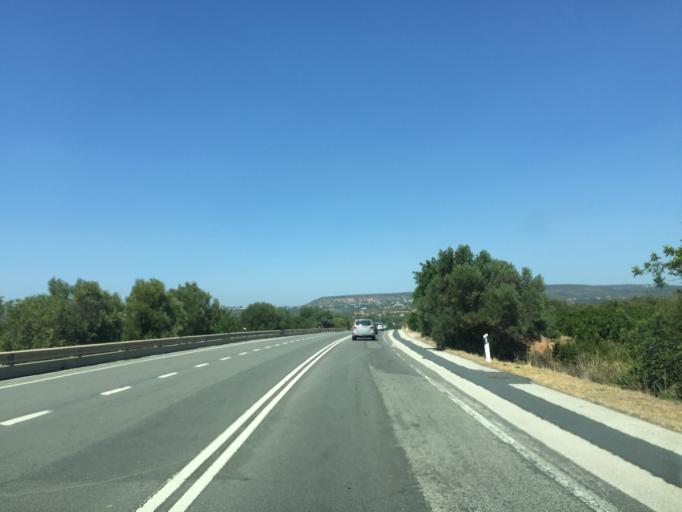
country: PT
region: Faro
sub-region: Silves
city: Sao Bartolomeu de Messines
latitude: 37.2001
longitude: -8.2612
